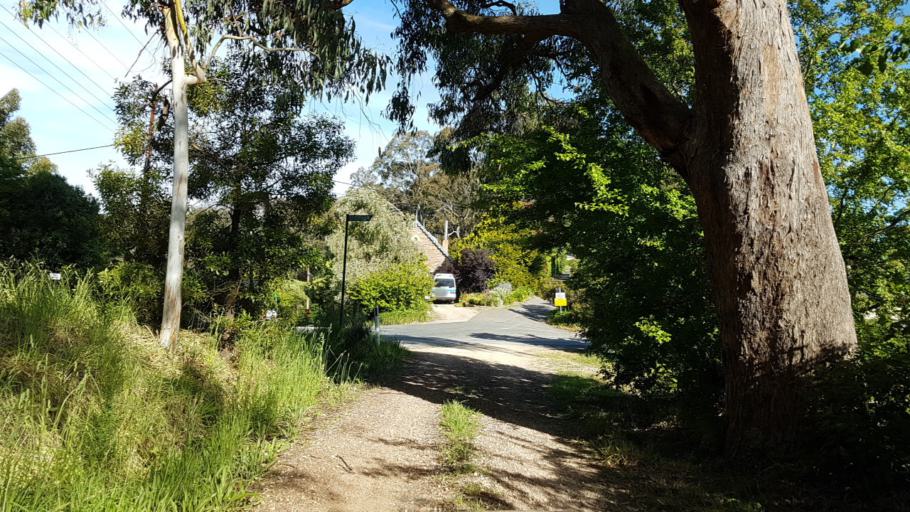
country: AU
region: South Australia
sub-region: Adelaide Hills
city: Adelaide Hills
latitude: -34.9117
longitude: 138.7652
